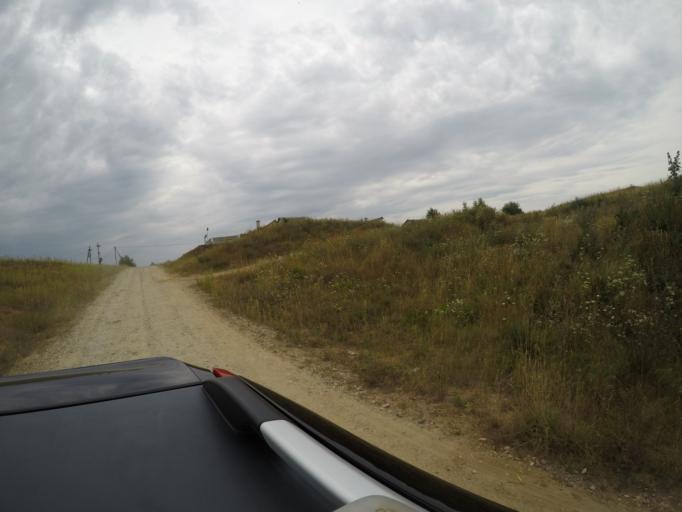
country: BY
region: Grodnenskaya
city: Hal'shany
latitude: 54.2594
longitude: 26.0055
